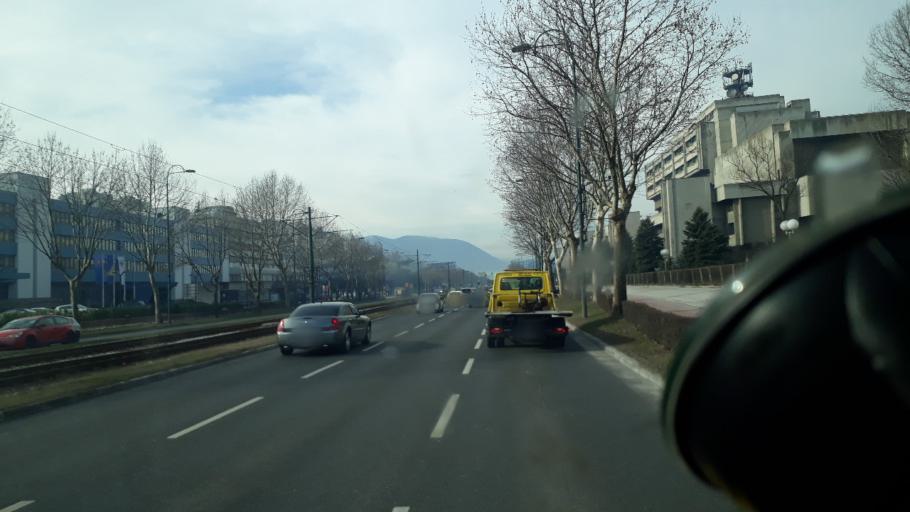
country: BA
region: Federation of Bosnia and Herzegovina
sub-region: Kanton Sarajevo
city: Sarajevo
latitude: 43.8450
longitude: 18.3578
